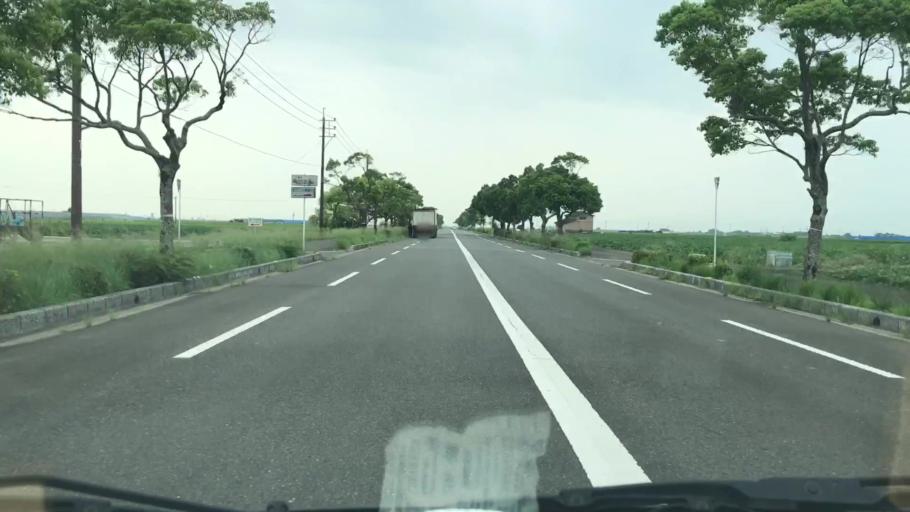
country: JP
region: Saga Prefecture
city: Okawa
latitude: 33.1882
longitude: 130.3018
